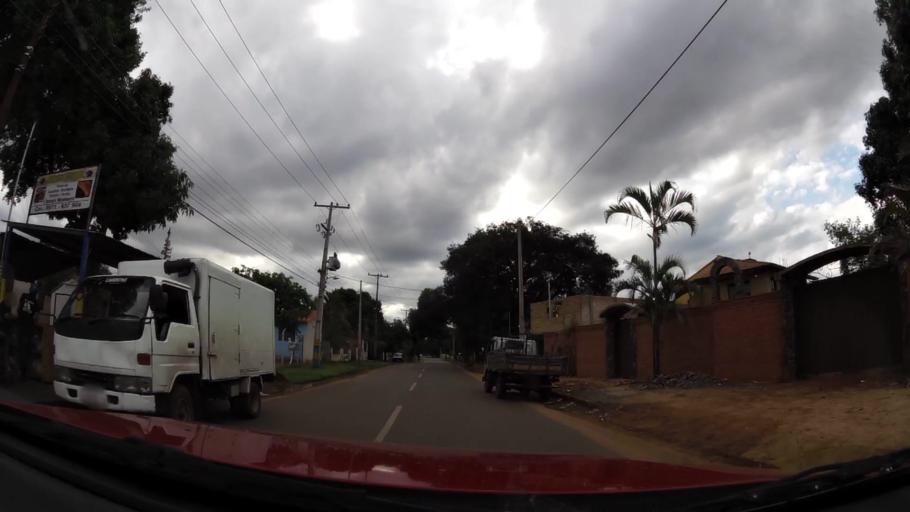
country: PY
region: Central
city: San Lorenzo
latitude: -25.2901
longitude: -57.4829
